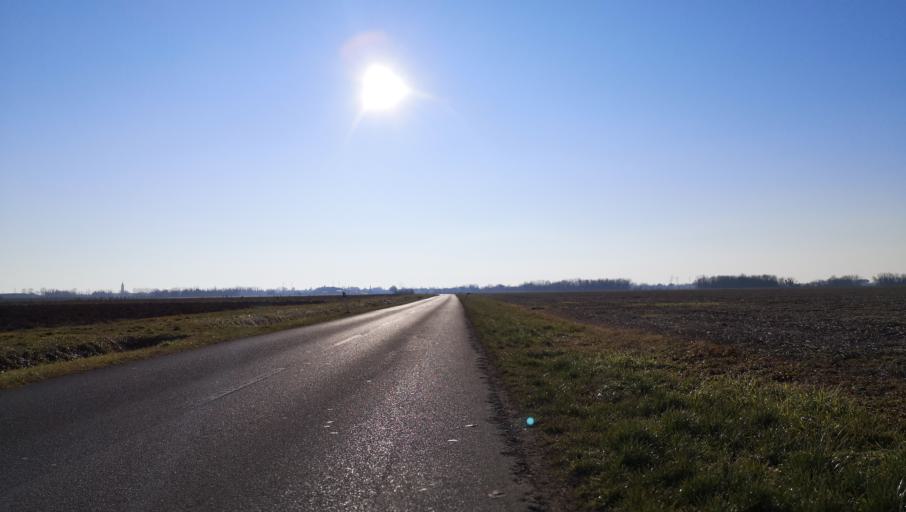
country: IT
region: Friuli Venezia Giulia
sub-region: Provincia di Udine
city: Santa Maria la Longa
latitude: 45.9479
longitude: 13.2733
